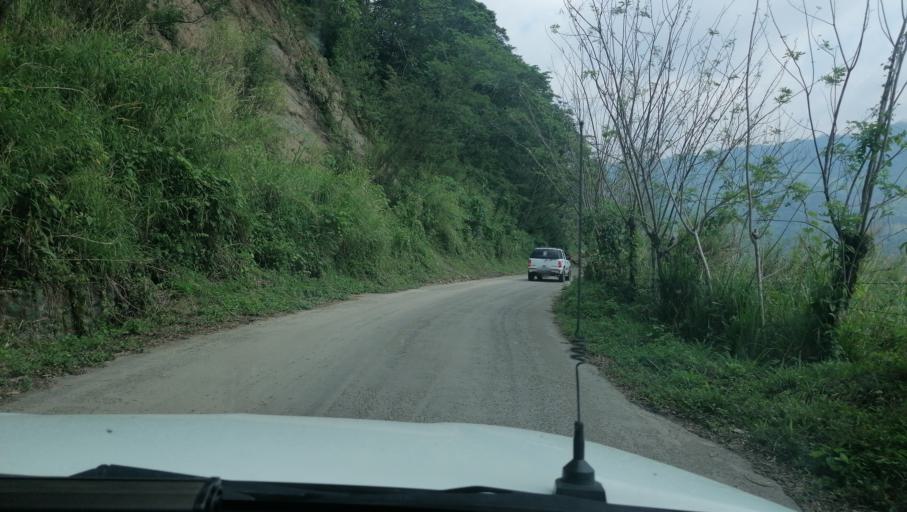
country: MX
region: Chiapas
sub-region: Francisco Leon
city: San Miguel la Sardina
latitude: 17.2296
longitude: -93.3502
